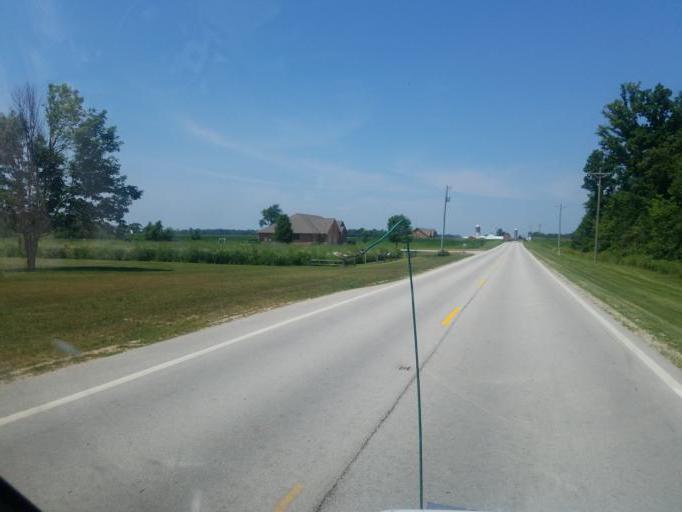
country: US
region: Ohio
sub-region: Shelby County
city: Fort Loramie
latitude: 40.3464
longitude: -84.4346
